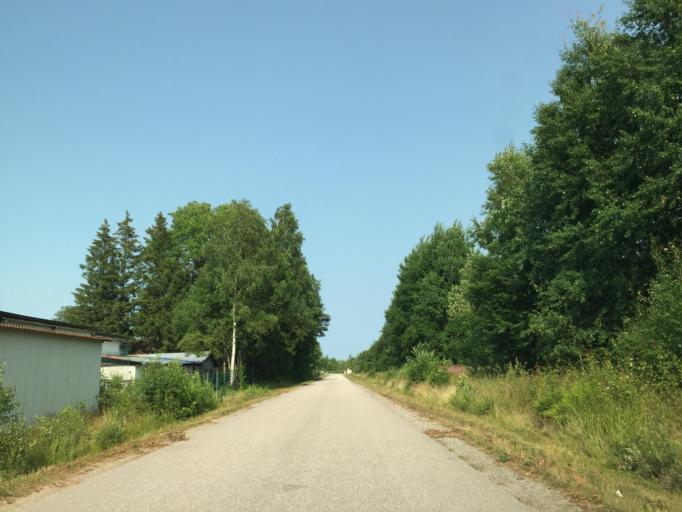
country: SE
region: Vaestra Goetaland
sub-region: Vanersborgs Kommun
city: Vanersborg
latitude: 58.3550
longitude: 12.2671
